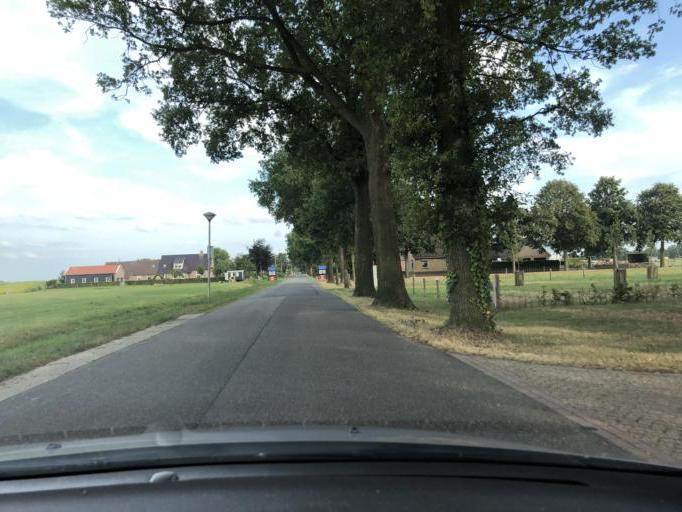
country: NL
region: Overijssel
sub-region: Gemeente Staphorst
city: Staphorst
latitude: 52.6123
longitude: 6.2657
